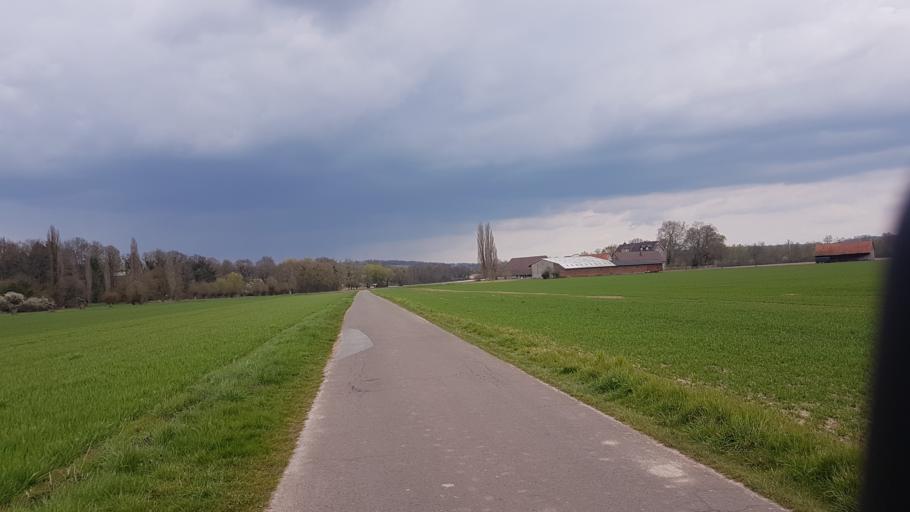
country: DE
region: Lower Saxony
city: Hessisch Oldendorf
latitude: 52.1587
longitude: 9.2813
